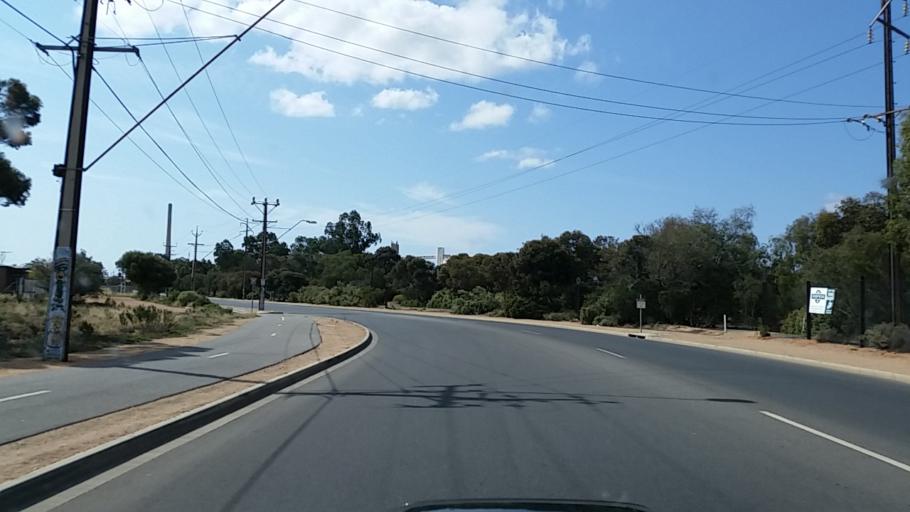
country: AU
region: South Australia
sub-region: Port Pirie City and Dists
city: Port Pirie
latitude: -33.1874
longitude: 138.0115
